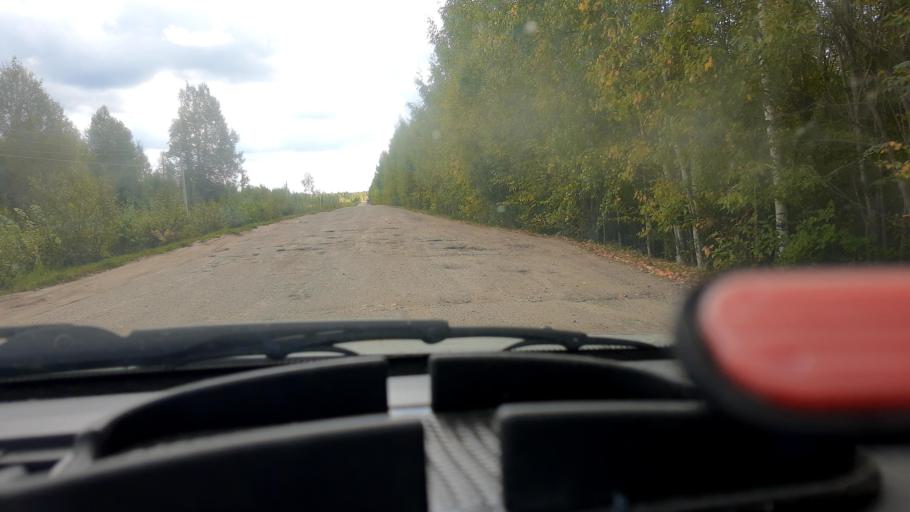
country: RU
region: Mariy-El
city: Kilemary
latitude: 56.8908
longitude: 46.7560
